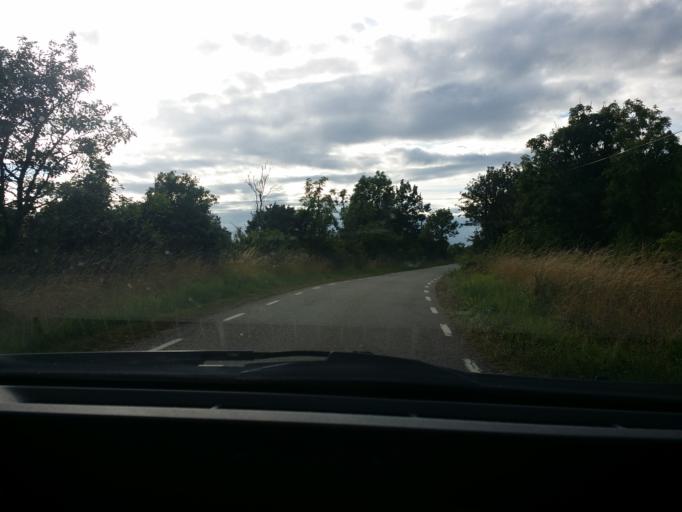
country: SE
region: Kalmar
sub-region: Borgholms Kommun
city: Borgholm
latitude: 57.1135
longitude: 16.9784
